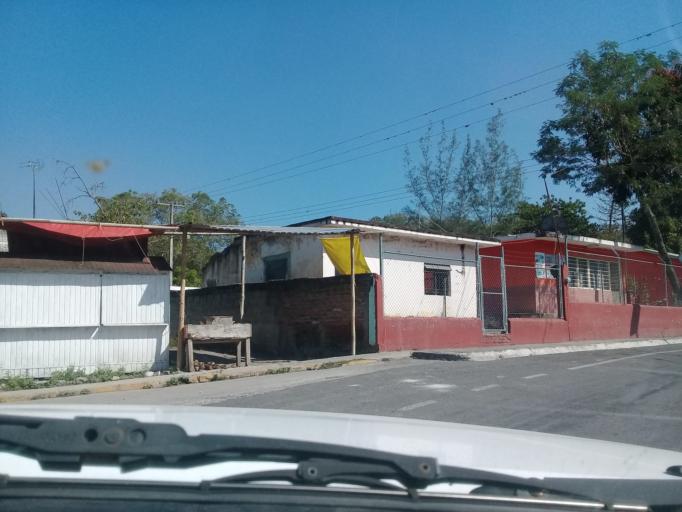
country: MX
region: Veracruz
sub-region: Emiliano Zapata
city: Plan del Rio
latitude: 19.4185
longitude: -96.6163
